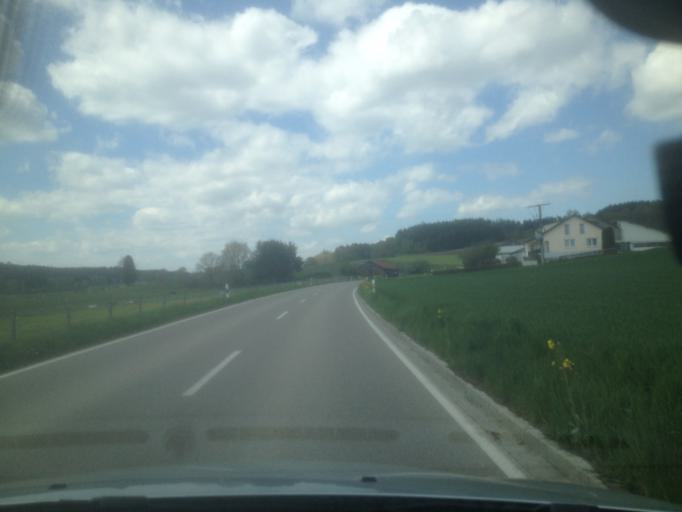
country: DE
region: Bavaria
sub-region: Swabia
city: Altenmunster
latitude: 48.4628
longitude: 10.5819
